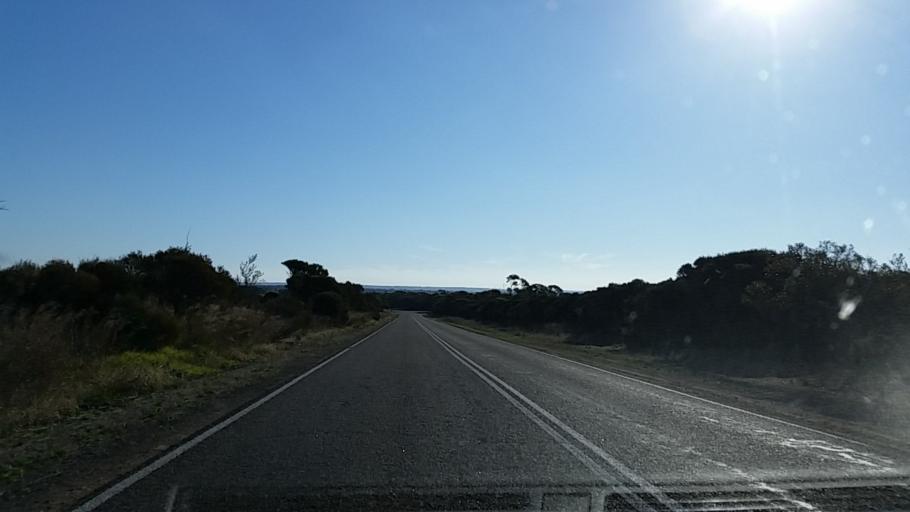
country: AU
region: South Australia
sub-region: Murray Bridge
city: Murray Bridge
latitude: -35.1249
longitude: 139.1857
